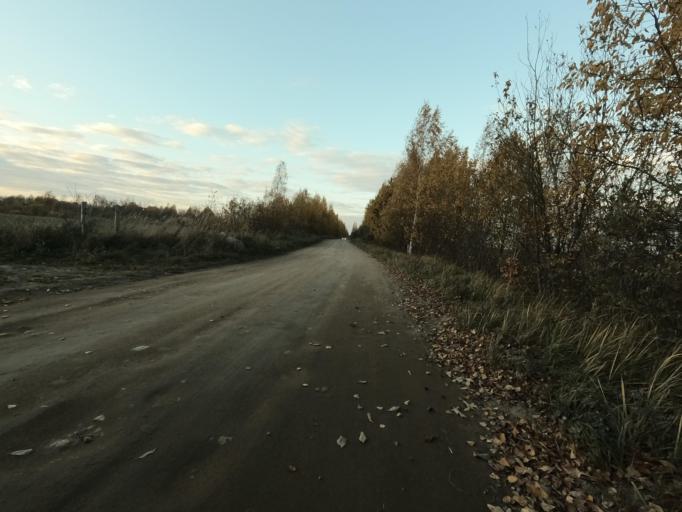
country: RU
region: Leningrad
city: Mga
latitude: 59.7917
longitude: 31.2012
